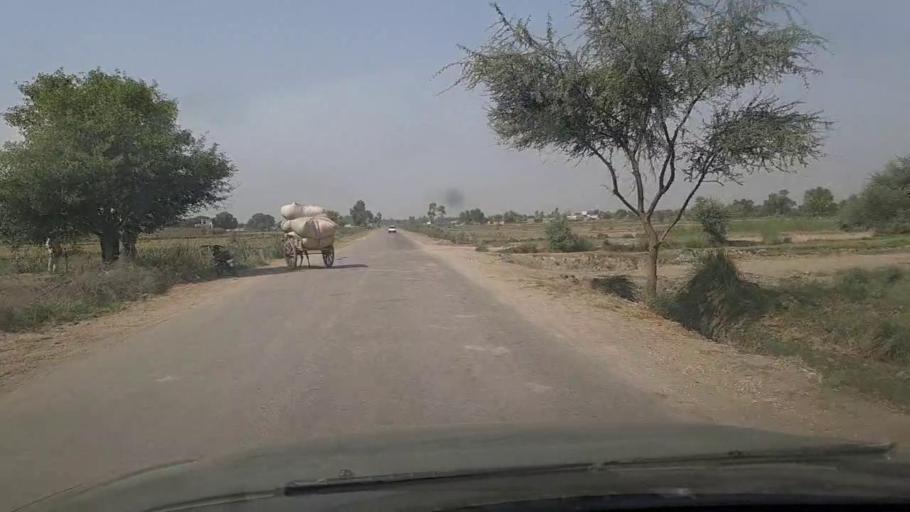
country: PK
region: Sindh
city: Khanpur
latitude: 27.8998
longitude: 69.4958
